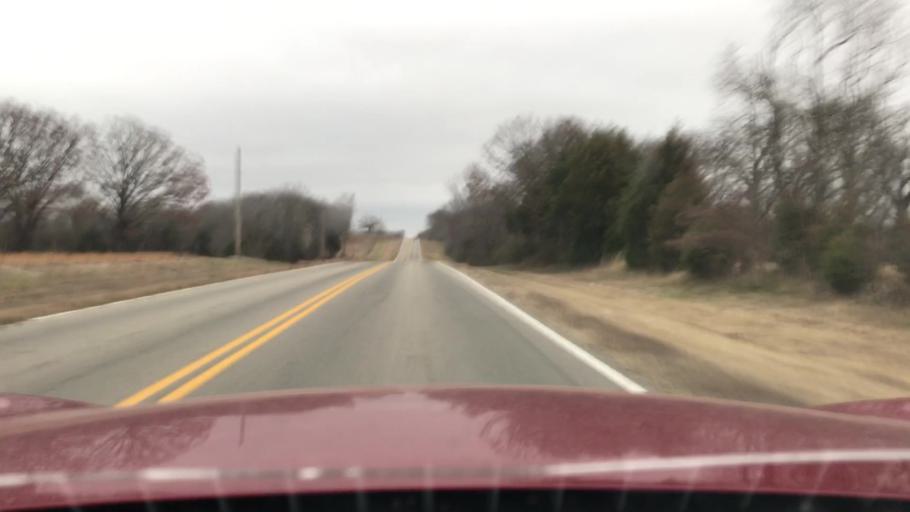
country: US
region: Oklahoma
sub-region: Sequoyah County
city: Sallisaw
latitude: 35.5070
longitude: -94.7594
